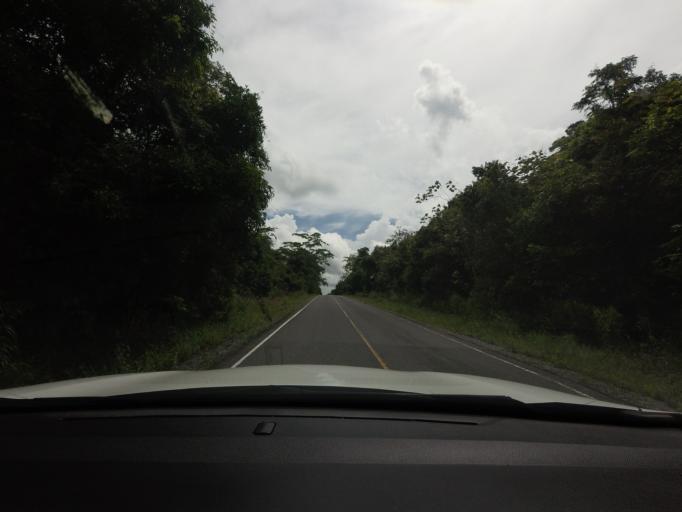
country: TH
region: Nakhon Nayok
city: Nakhon Nayok
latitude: 14.3966
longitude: 101.3641
